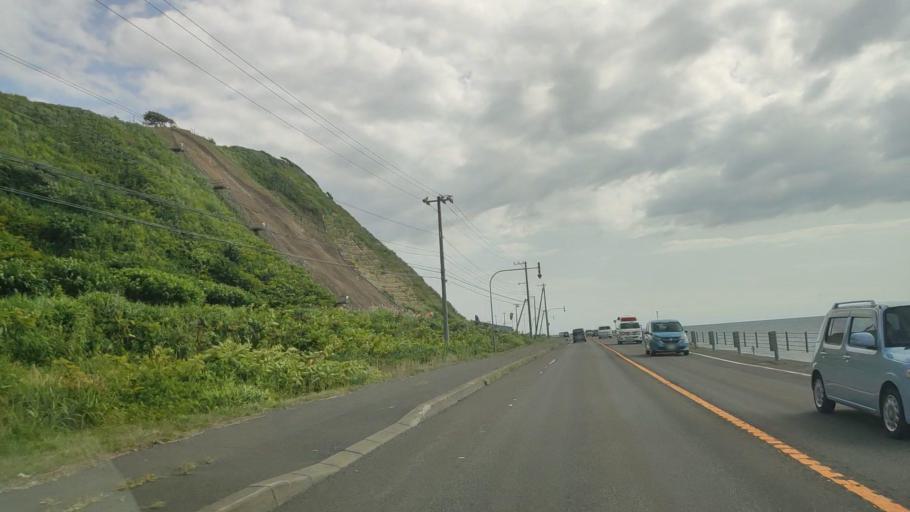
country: JP
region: Hokkaido
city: Rumoi
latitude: 44.2145
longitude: 141.6563
